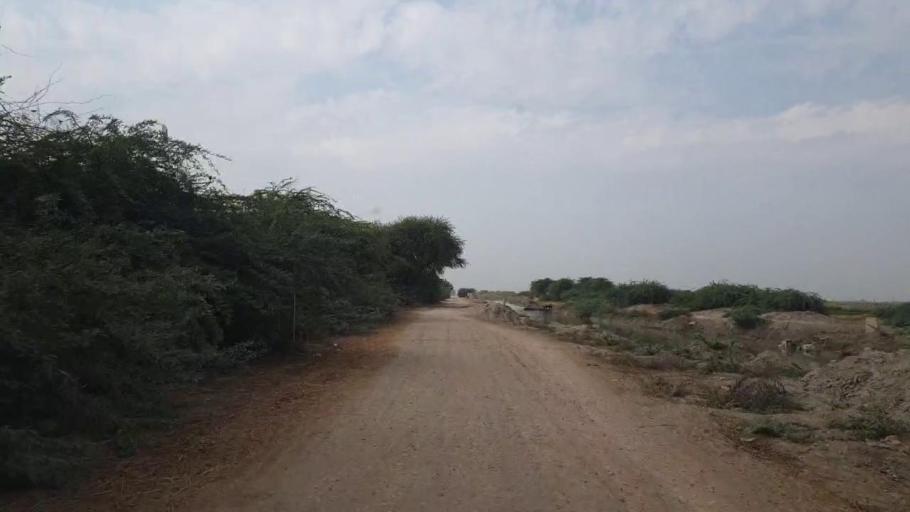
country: PK
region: Sindh
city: Kario
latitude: 24.6220
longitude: 68.5807
